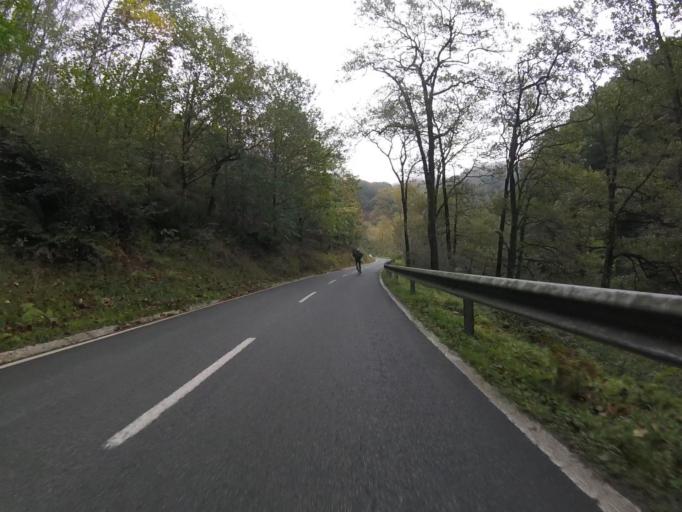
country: ES
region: Navarre
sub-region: Provincia de Navarra
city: Goizueta
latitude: 43.1982
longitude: -1.8589
